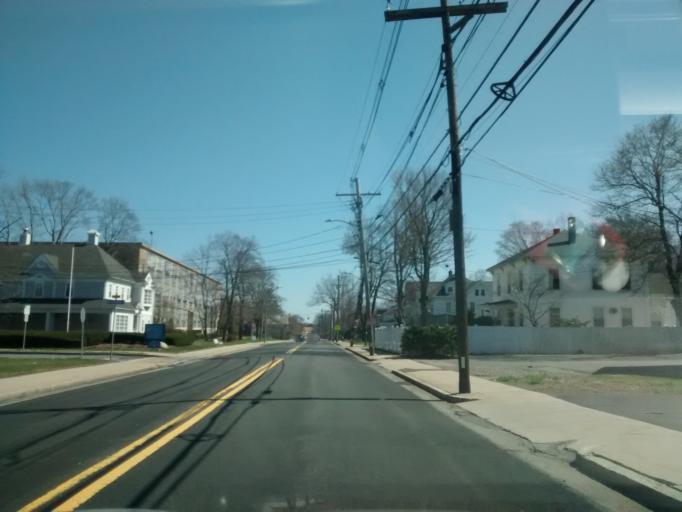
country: US
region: Massachusetts
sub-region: Middlesex County
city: Framingham
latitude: 42.2871
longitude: -71.4231
